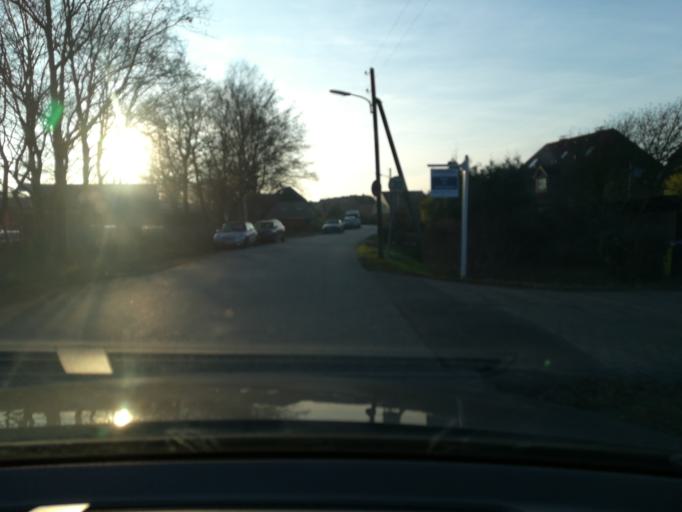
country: DE
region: Lower Saxony
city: Drage
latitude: 53.4224
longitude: 10.2048
